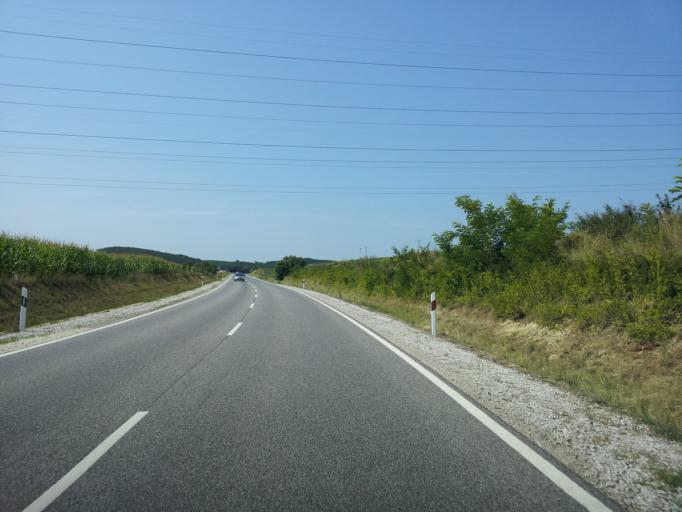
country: HU
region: Zala
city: Pacsa
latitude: 46.8304
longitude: 17.0181
